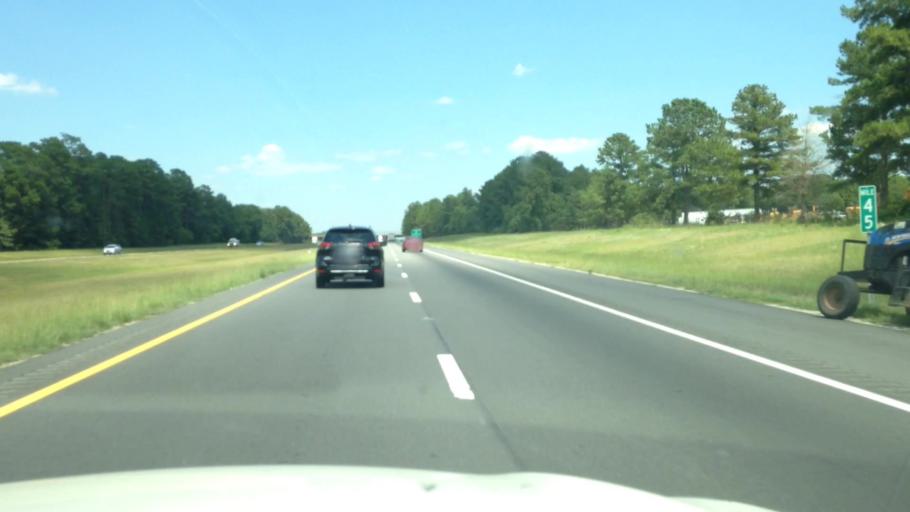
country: US
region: North Carolina
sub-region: Cumberland County
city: Hope Mills
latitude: 34.9706
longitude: -78.8716
